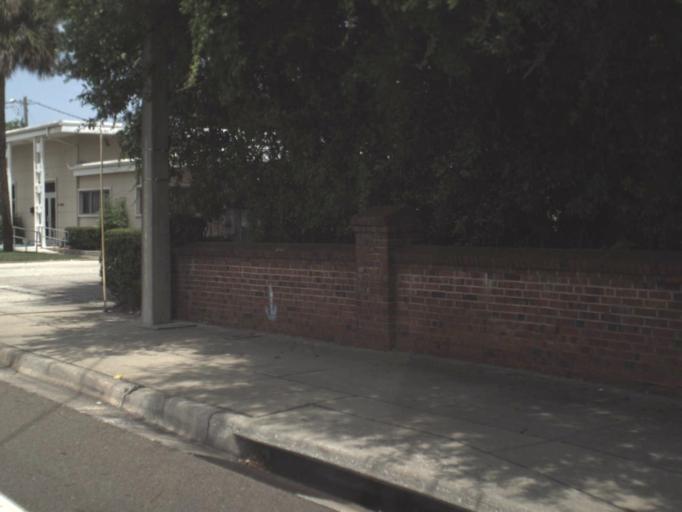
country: US
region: Florida
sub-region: Duval County
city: Jacksonville
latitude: 30.3675
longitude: -81.6524
